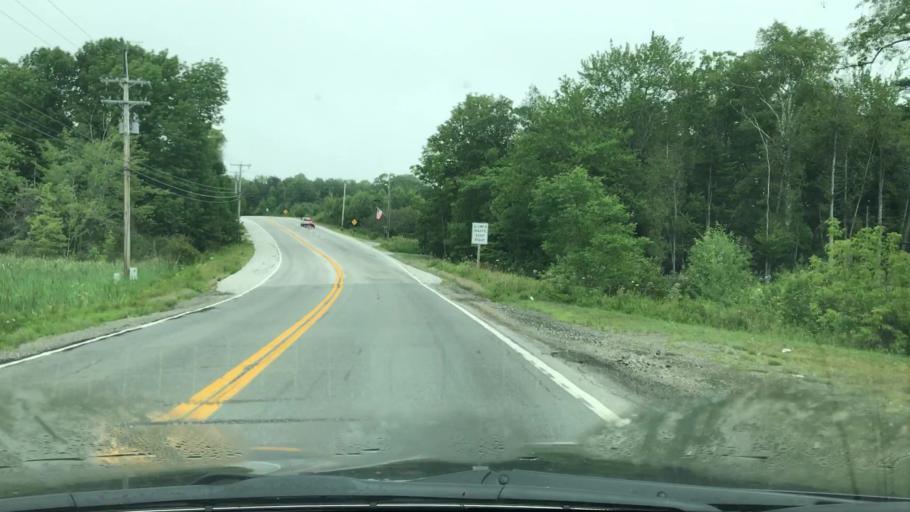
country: US
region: Maine
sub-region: Waldo County
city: Lincolnville
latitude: 44.3025
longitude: -68.9808
